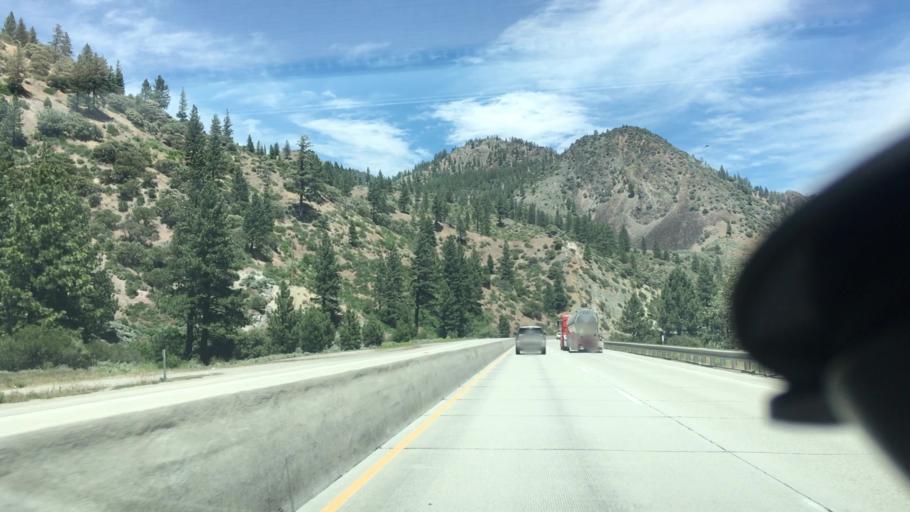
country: US
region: Nevada
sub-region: Washoe County
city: Verdi
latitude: 39.4282
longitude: -120.0344
